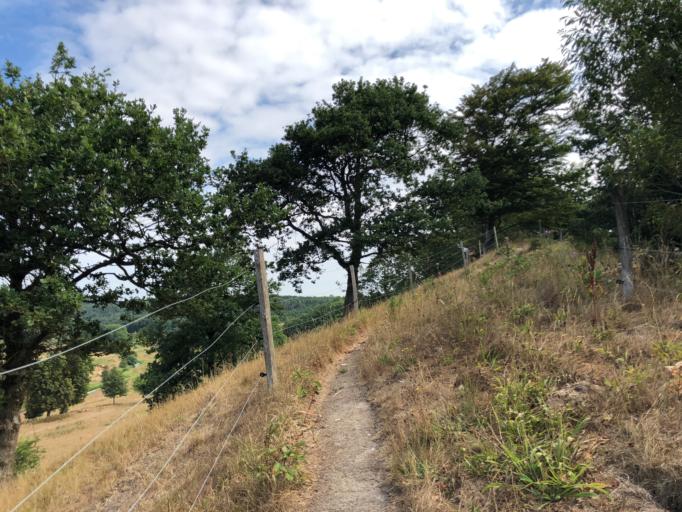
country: DK
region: South Denmark
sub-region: Vejle Kommune
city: Egtved
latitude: 55.6529
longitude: 9.2868
